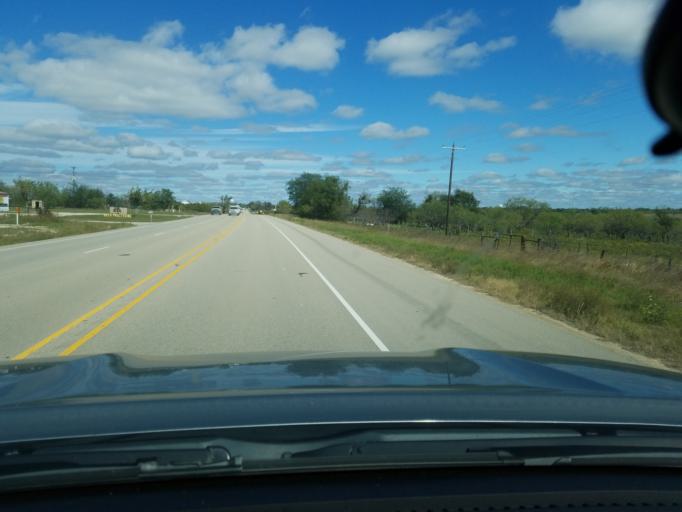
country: US
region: Texas
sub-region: Hamilton County
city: Hamilton
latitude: 31.6820
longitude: -98.1325
